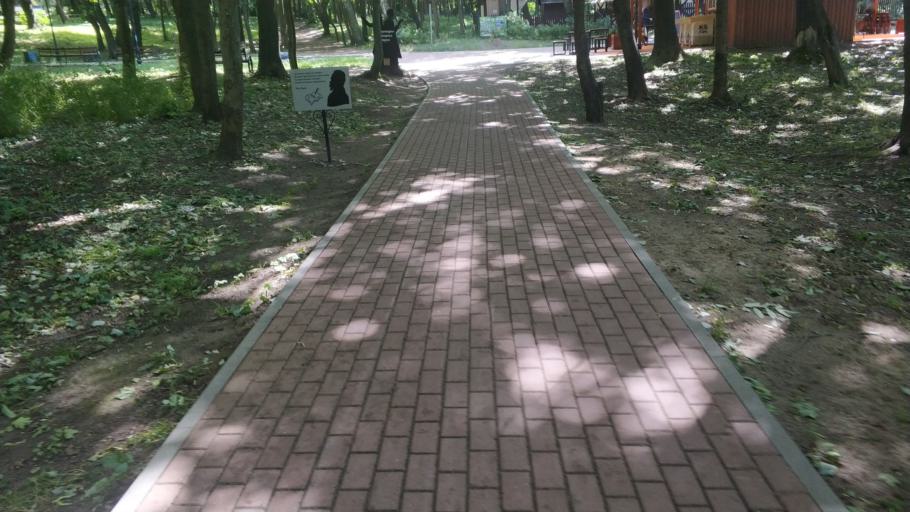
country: RU
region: Kaliningrad
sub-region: Gorod Kaliningrad
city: Yantarnyy
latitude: 54.8674
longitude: 19.9345
